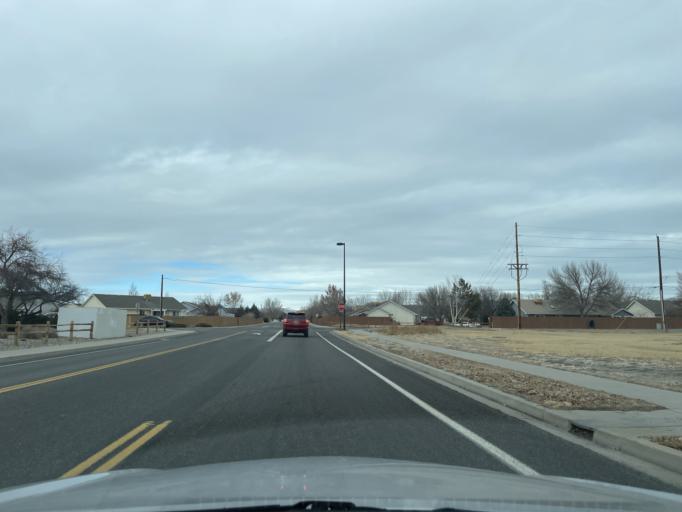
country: US
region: Colorado
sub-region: Mesa County
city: Grand Junction
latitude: 39.0984
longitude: -108.5801
